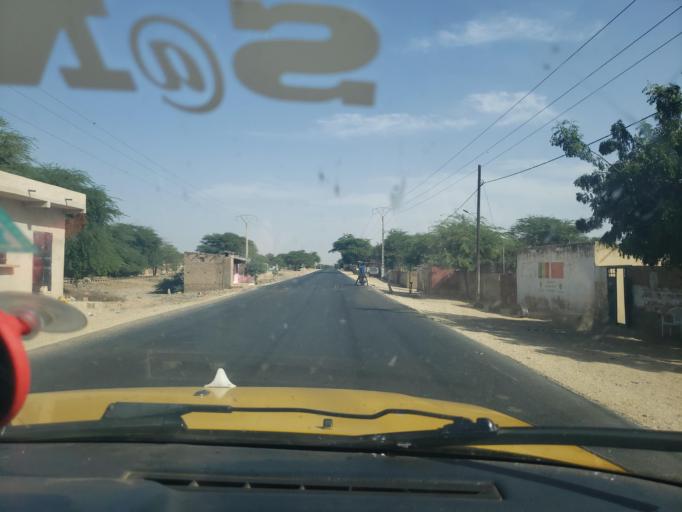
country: SN
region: Saint-Louis
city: Saint-Louis
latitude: 15.9282
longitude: -16.3238
